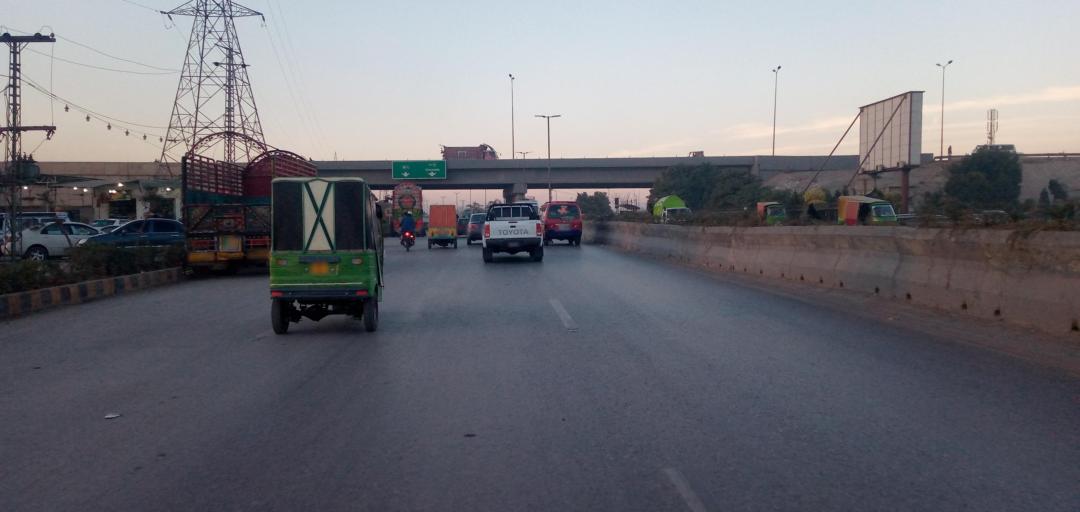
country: PK
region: Khyber Pakhtunkhwa
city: Peshawar
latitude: 34.0227
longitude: 71.6211
